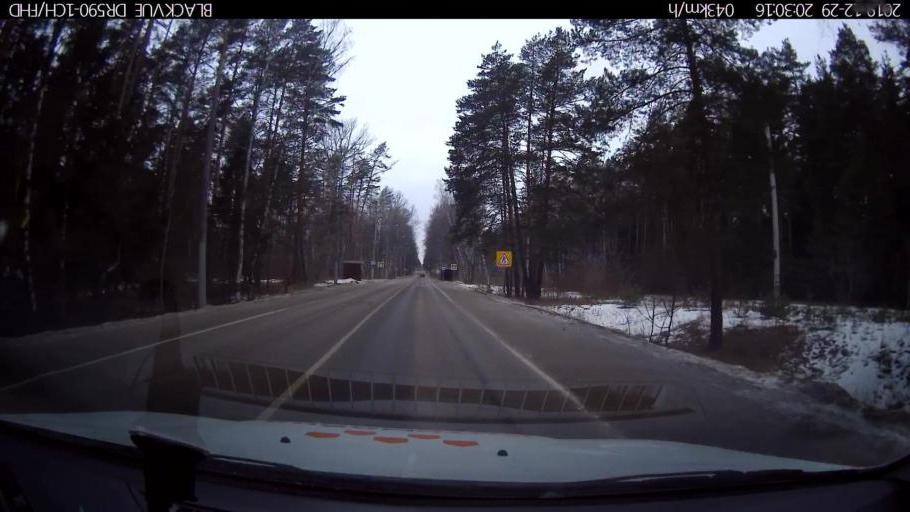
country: RU
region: Nizjnij Novgorod
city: Afonino
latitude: 56.1745
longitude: 44.0971
